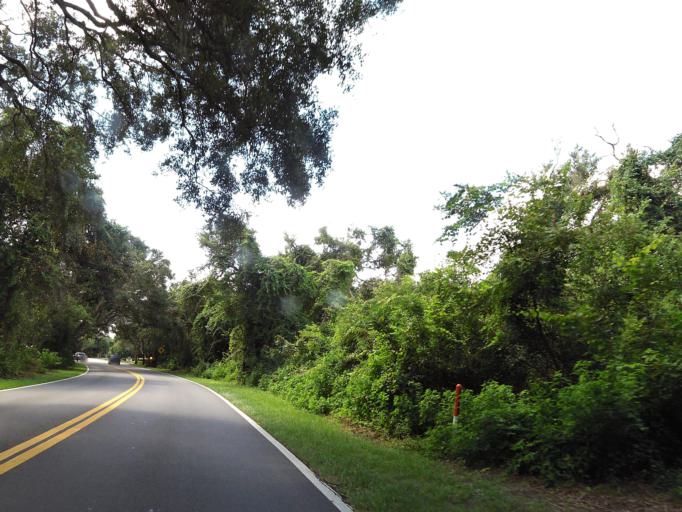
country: US
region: Florida
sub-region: Nassau County
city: Fernandina Beach
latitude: 30.5953
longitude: -81.4473
